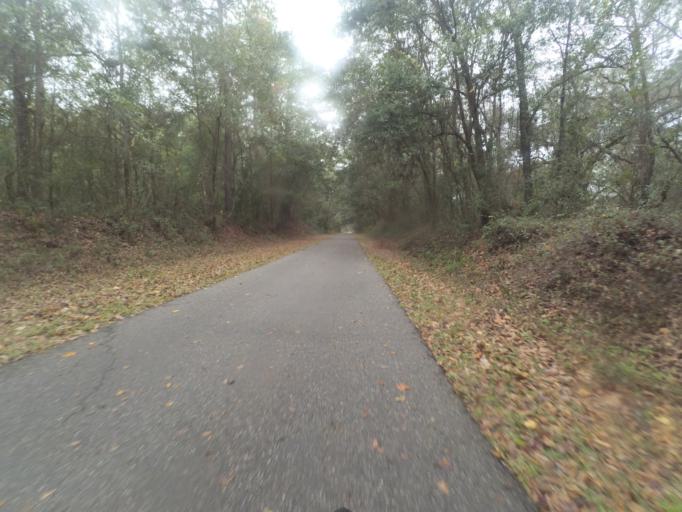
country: US
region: Florida
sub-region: Alachua County
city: Hawthorne
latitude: 29.5954
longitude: -82.1391
